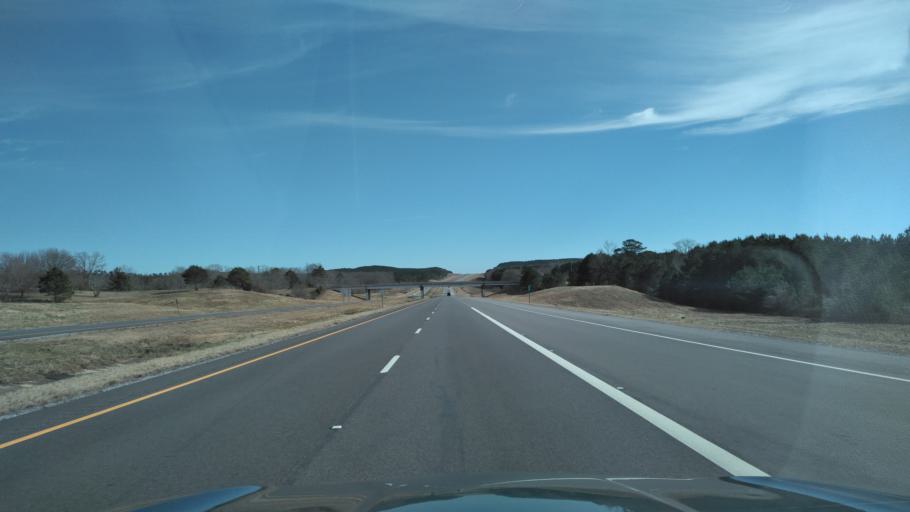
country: US
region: Alabama
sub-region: Walker County
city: Carbon Hill
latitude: 33.9507
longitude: -87.6108
